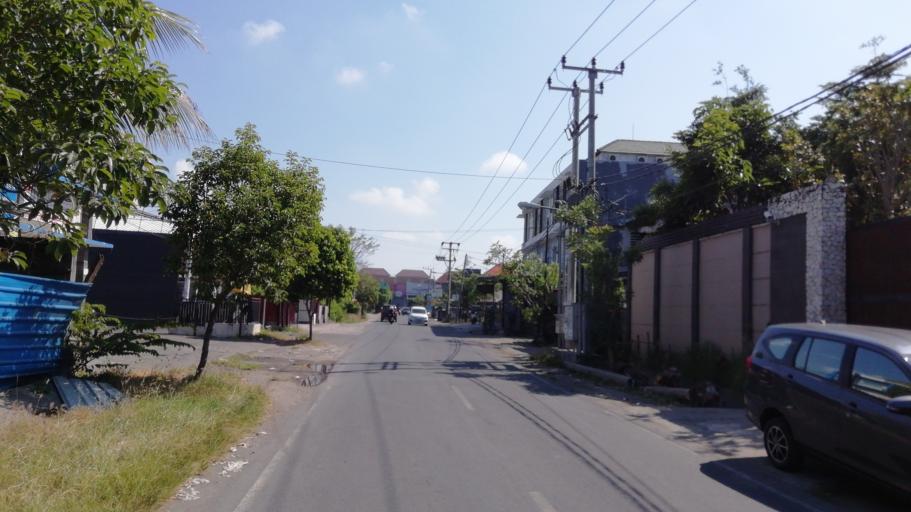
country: ID
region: Bali
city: Banjar Taman
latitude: -8.6790
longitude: 115.2378
